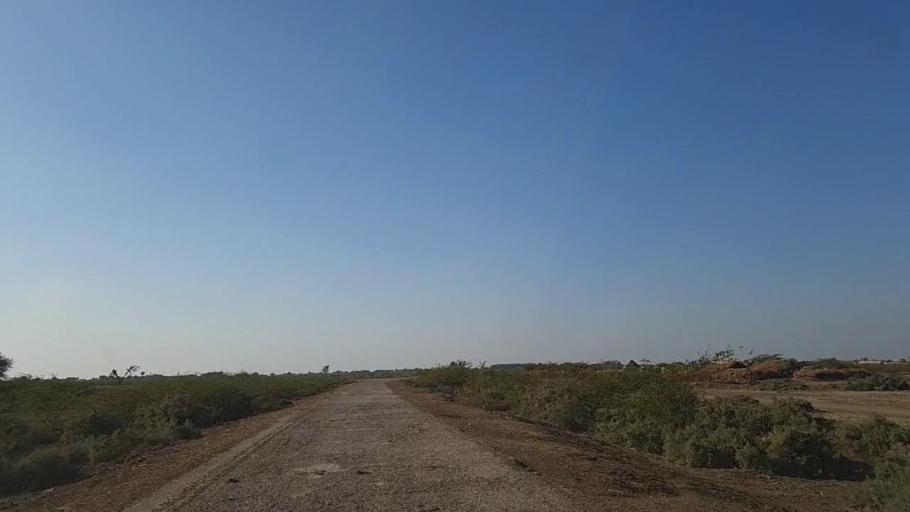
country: PK
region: Sindh
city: Samaro
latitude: 25.3552
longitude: 69.3788
